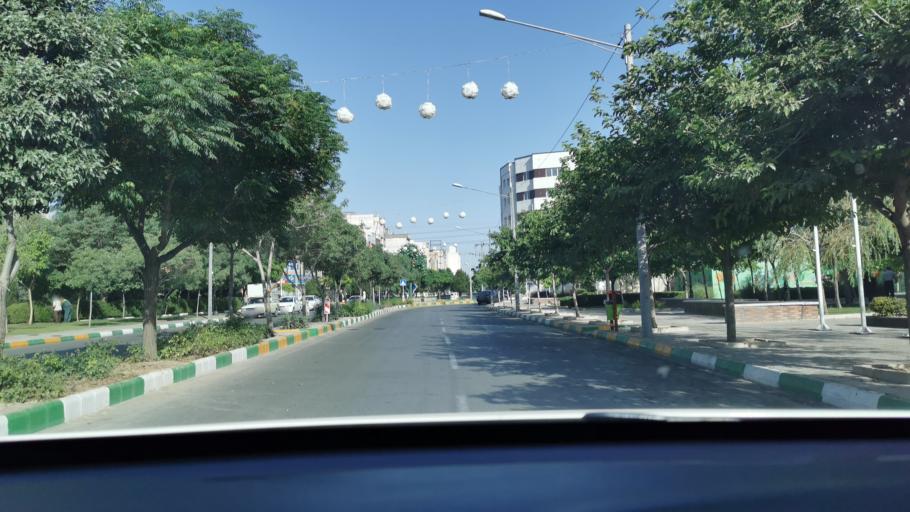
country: IR
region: Razavi Khorasan
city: Mashhad
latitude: 36.3385
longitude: 59.5080
